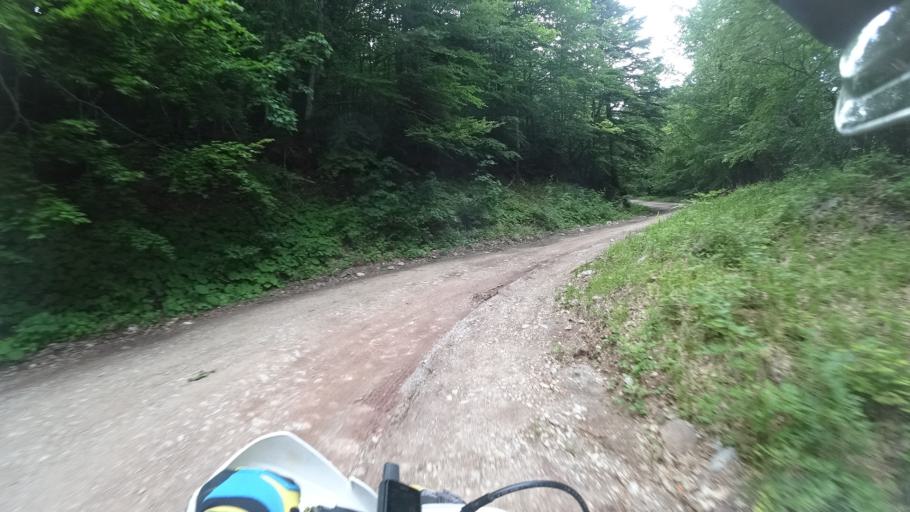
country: HR
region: Licko-Senjska
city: Gospic
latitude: 44.4658
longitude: 15.2999
